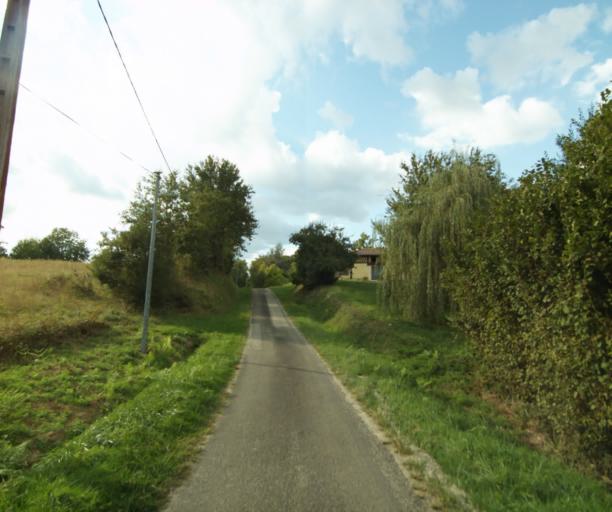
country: FR
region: Midi-Pyrenees
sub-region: Departement du Gers
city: Cazaubon
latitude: 43.8946
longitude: -0.0926
